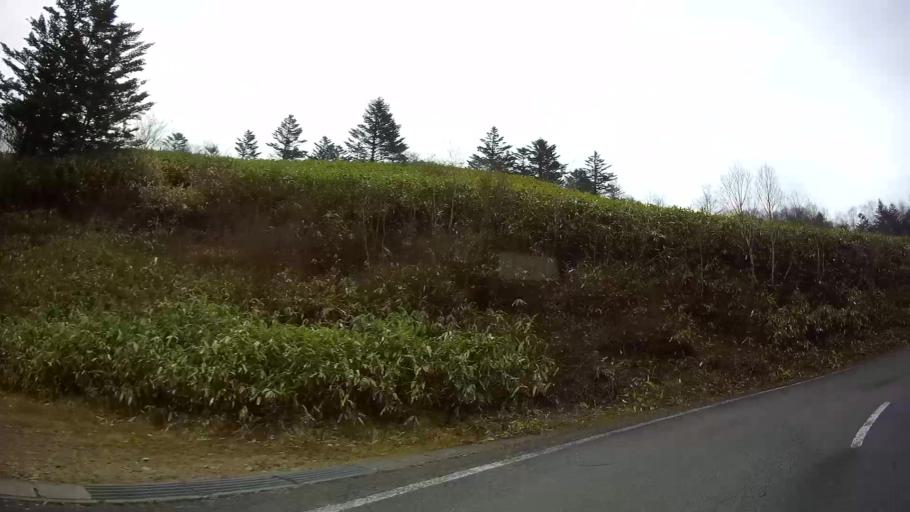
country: JP
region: Gunma
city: Nakanojomachi
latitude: 36.7198
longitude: 138.6437
